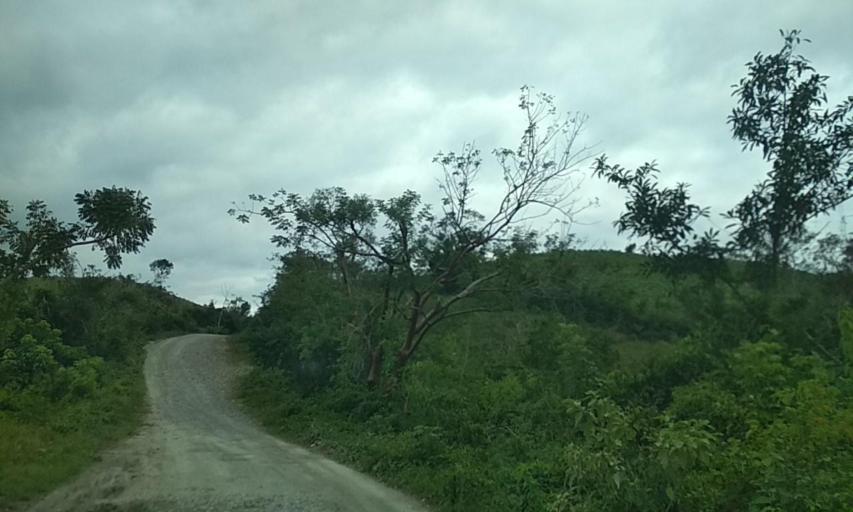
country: MX
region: Veracruz
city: Papantla de Olarte
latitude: 20.4807
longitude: -97.3097
